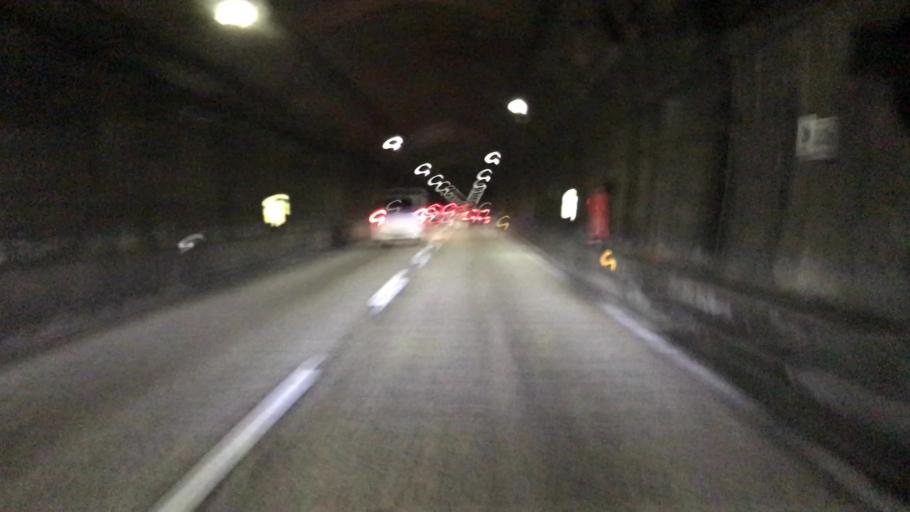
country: JP
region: Hyogo
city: Kobe
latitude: 34.7299
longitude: 135.1798
